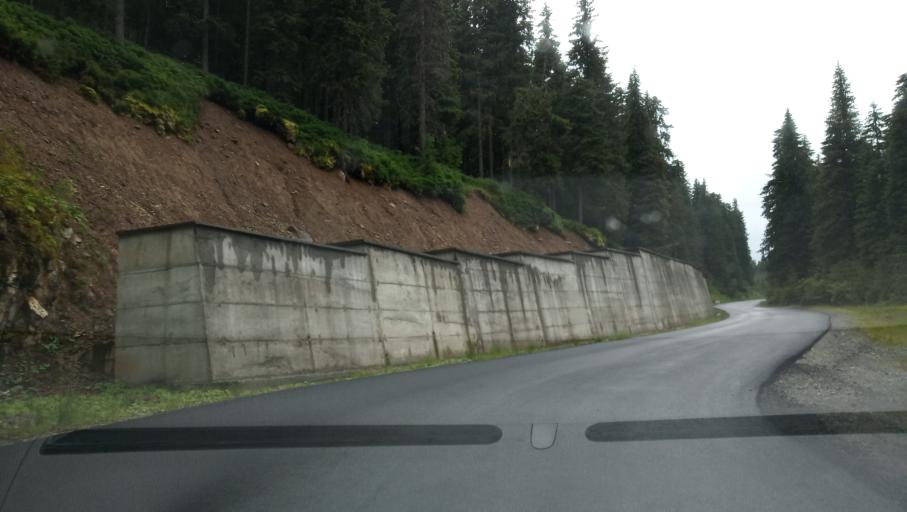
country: RO
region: Hunedoara
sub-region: Oras Petrila
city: Petrila
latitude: 45.4127
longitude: 23.6009
